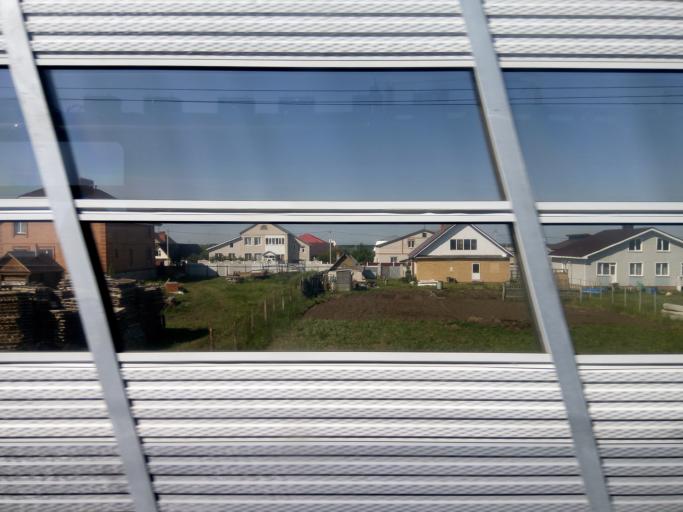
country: RU
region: Tatarstan
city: Stolbishchi
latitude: 55.6620
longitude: 49.2221
